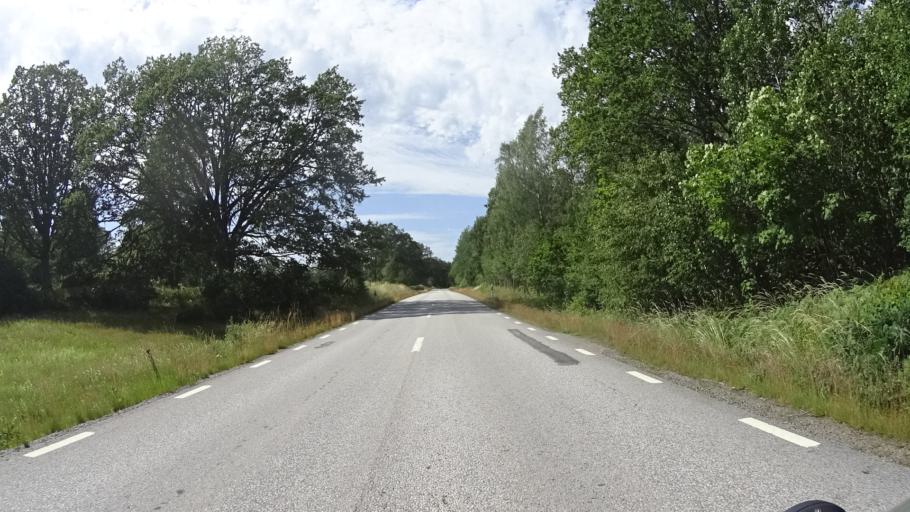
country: SE
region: OEstergoetland
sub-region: Atvidabergs Kommun
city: Atvidaberg
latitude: 58.0925
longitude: 16.1318
